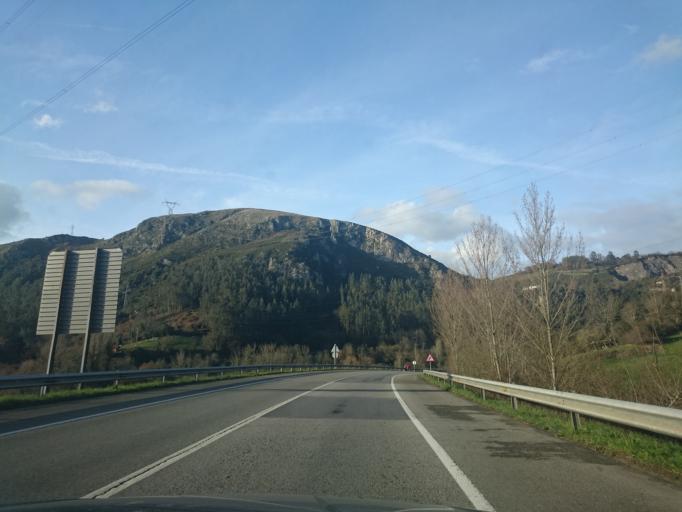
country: ES
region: Asturias
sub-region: Province of Asturias
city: Oviedo
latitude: 43.3037
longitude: -5.8297
